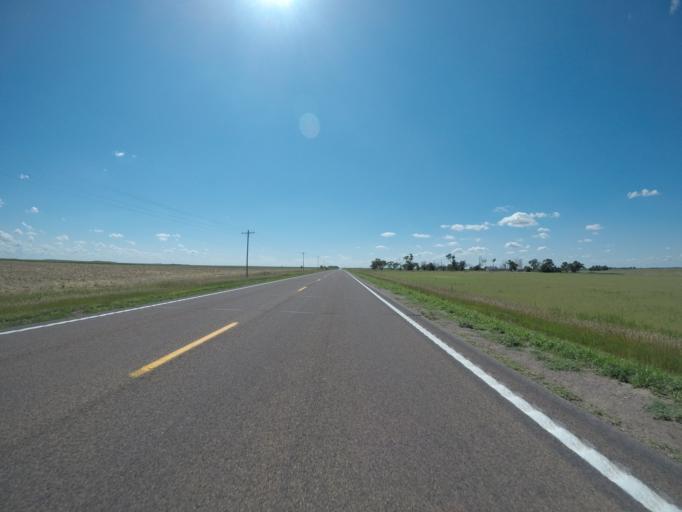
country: US
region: Nebraska
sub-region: Chase County
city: Imperial
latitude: 40.5377
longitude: -101.7061
